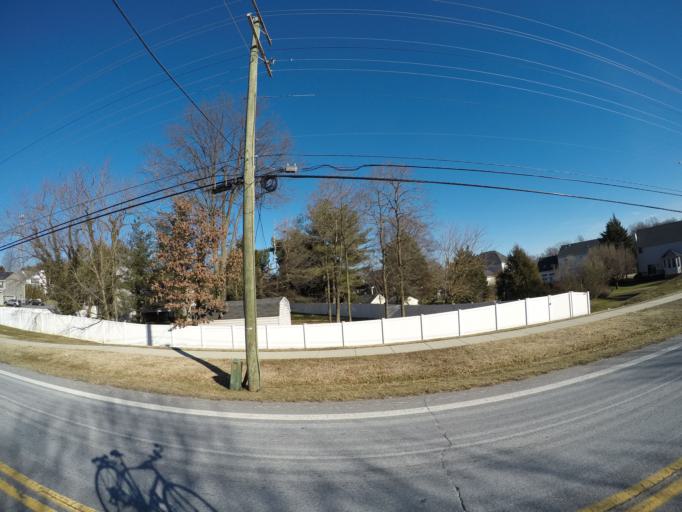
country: US
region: Maryland
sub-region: Howard County
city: Ilchester
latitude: 39.2243
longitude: -76.7897
